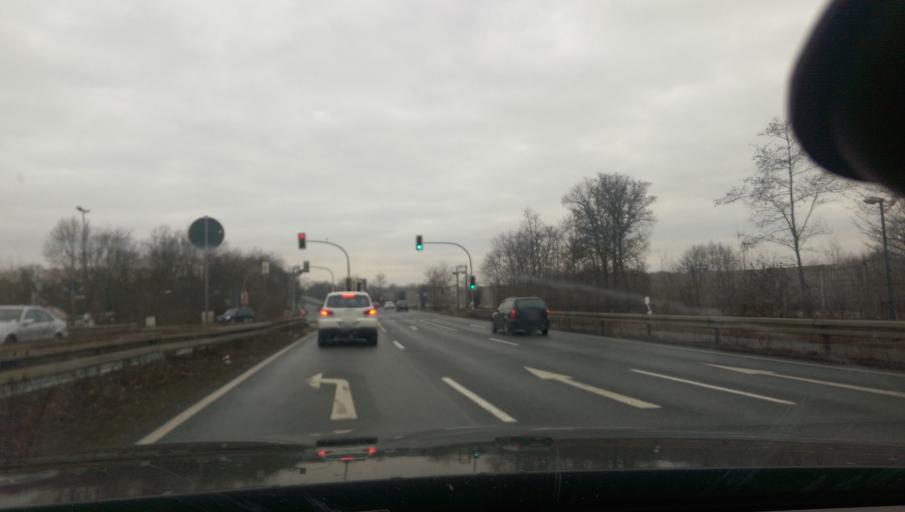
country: DE
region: Lower Saxony
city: Langenhagen
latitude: 52.4548
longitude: 9.7236
